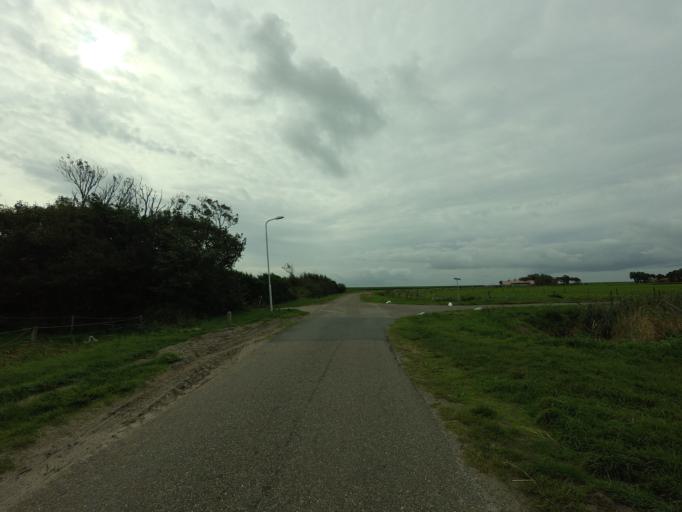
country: NL
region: Friesland
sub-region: Gemeente Ameland
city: Nes
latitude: 53.4363
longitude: 5.7065
